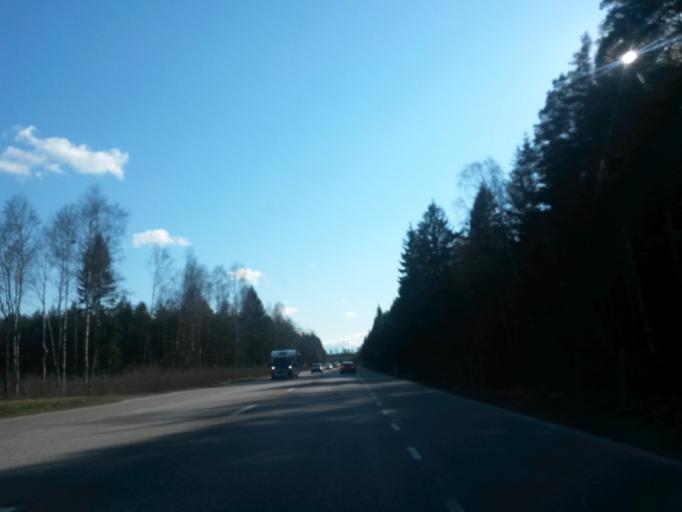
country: SE
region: Vaestra Goetaland
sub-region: Vara Kommun
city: Vara
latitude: 58.2237
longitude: 12.9203
